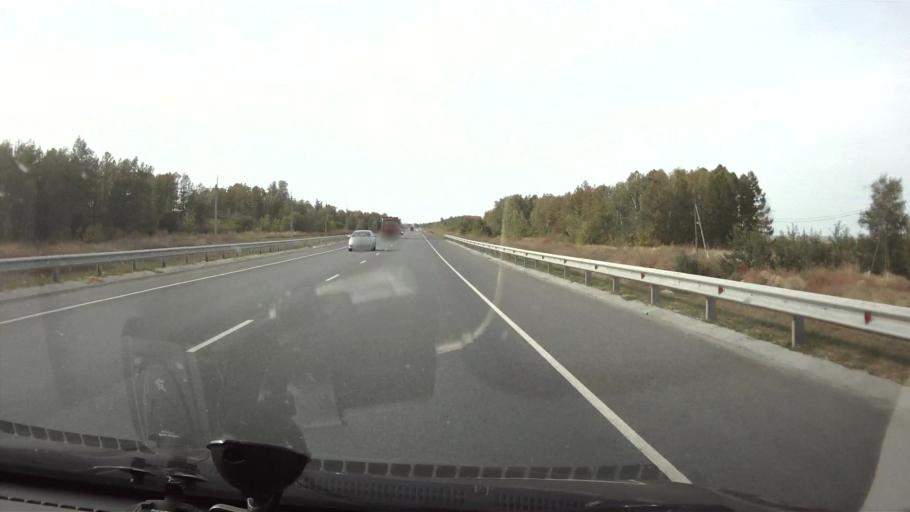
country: RU
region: Saratov
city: Shikhany
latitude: 52.1521
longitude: 47.1841
